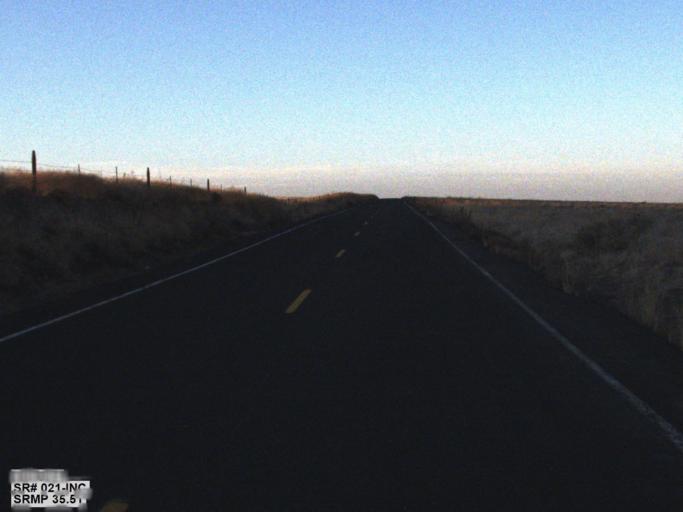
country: US
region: Washington
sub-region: Adams County
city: Ritzville
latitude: 47.0646
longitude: -118.6630
